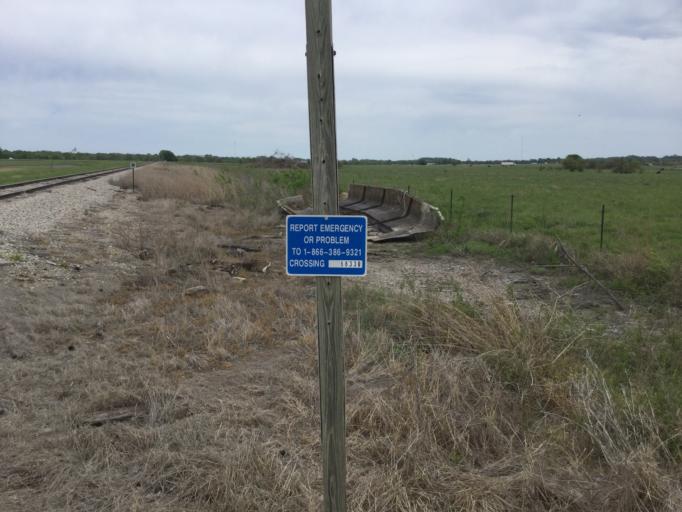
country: US
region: Kansas
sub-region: Montgomery County
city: Cherryvale
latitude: 37.2625
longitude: -95.5763
